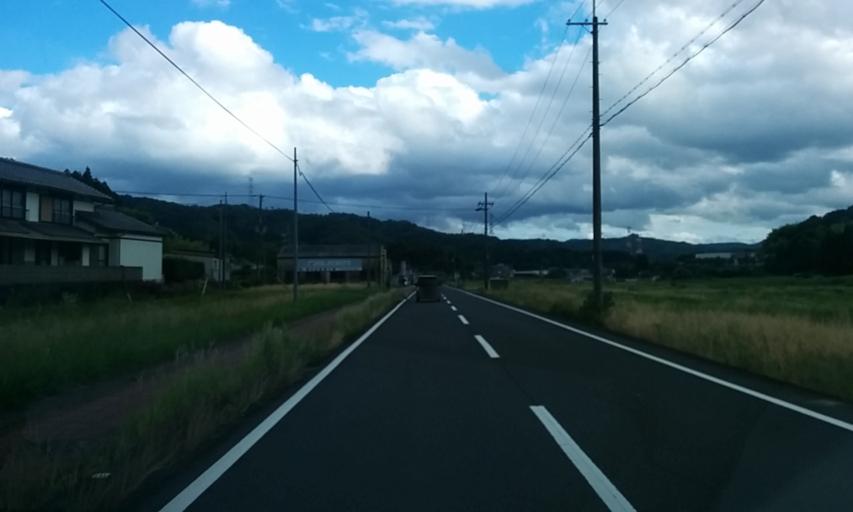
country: JP
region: Kyoto
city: Ayabe
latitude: 35.3331
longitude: 135.2925
